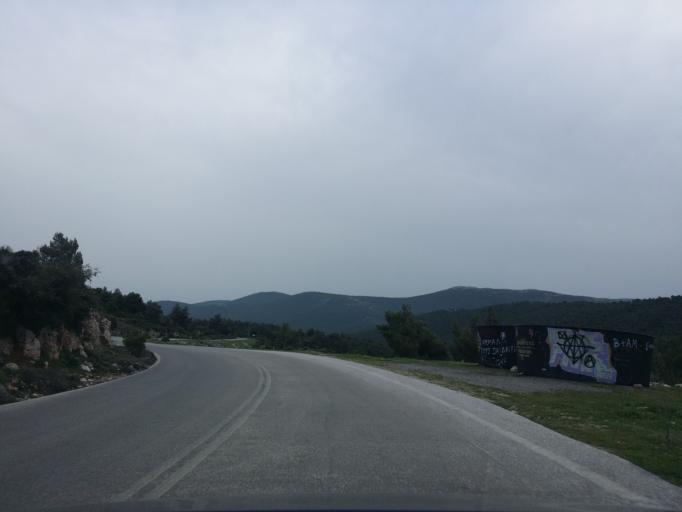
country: GR
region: Attica
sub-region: Nomarchia Dytikis Attikis
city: Vilia
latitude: 38.1688
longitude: 23.3172
